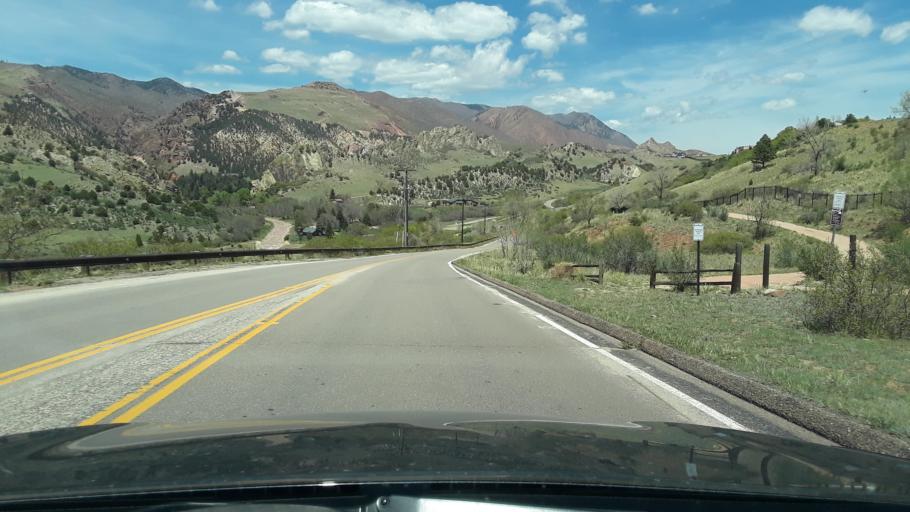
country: US
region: Colorado
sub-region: El Paso County
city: Manitou Springs
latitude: 38.8847
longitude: -104.8733
